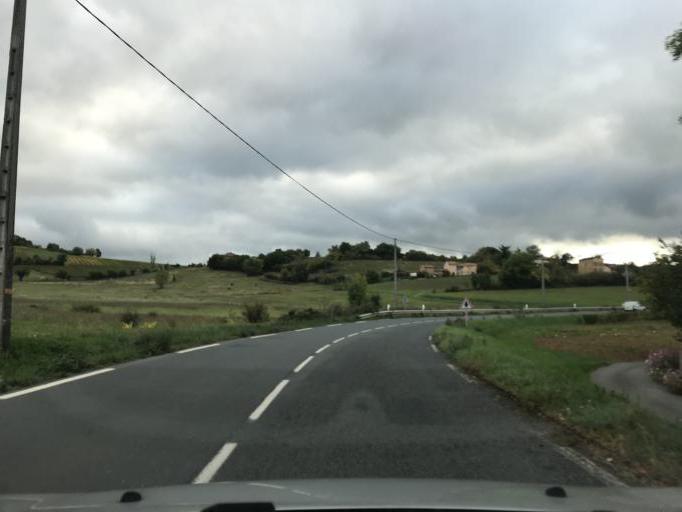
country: FR
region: Rhone-Alpes
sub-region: Departement du Rhone
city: Cogny
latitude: 45.9989
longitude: 4.6318
